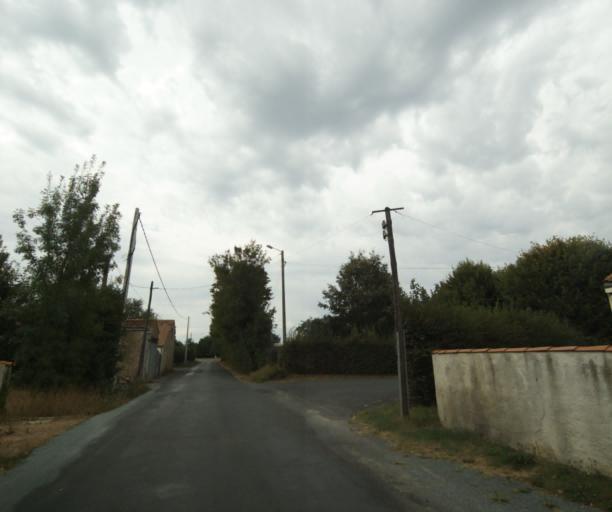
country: FR
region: Poitou-Charentes
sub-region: Departement de la Charente-Maritime
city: Tonnay-Charente
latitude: 45.9569
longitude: -0.8780
